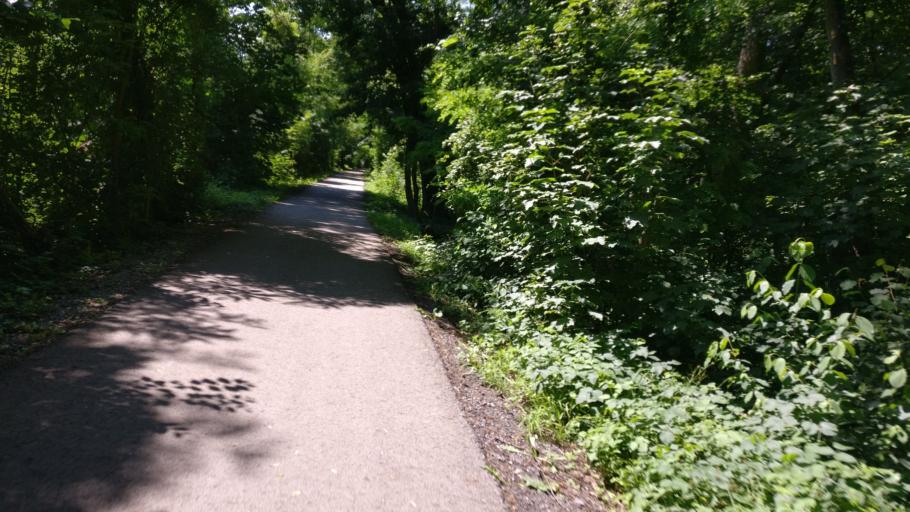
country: AT
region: Lower Austria
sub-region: Politischer Bezirk Baden
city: Tattendorf
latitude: 47.9621
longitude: 16.3099
